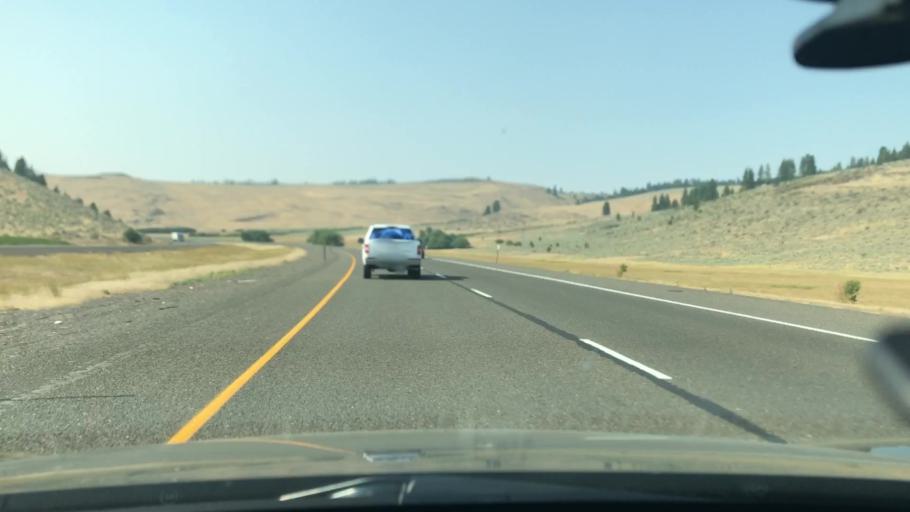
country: US
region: Oregon
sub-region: Union County
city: Union
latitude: 45.1645
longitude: -117.9642
